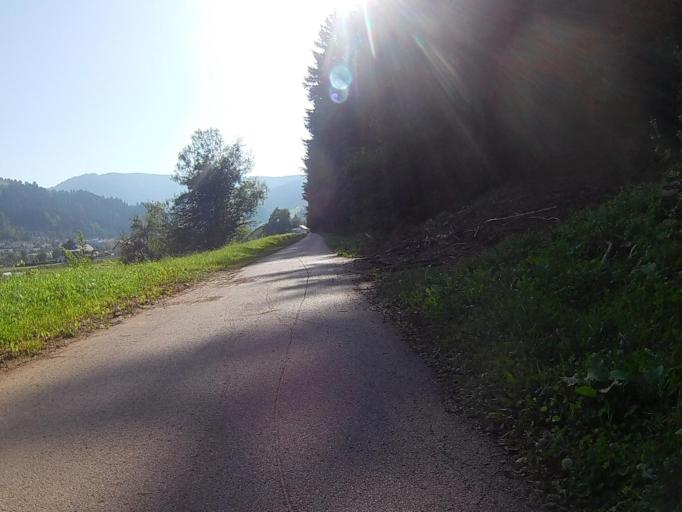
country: SI
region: Mislinja
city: Mislinja
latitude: 46.4437
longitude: 15.1866
